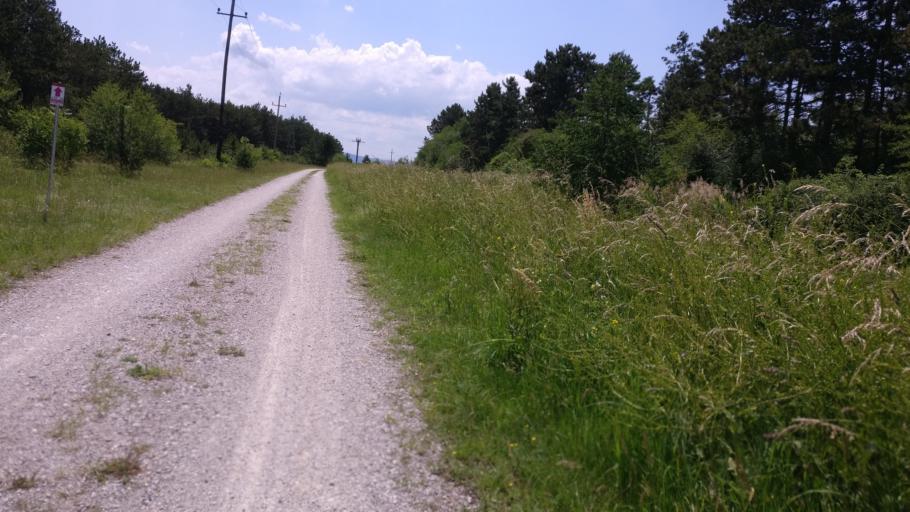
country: AT
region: Lower Austria
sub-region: Politischer Bezirk Wiener Neustadt
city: Lichtenworth
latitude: 47.8606
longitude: 16.2817
